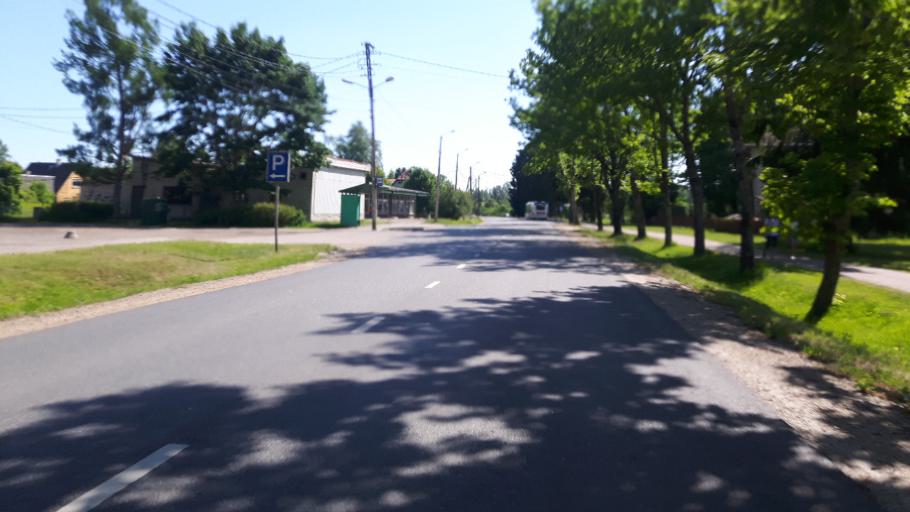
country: EE
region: Paernumaa
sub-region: Sindi linn
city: Sindi
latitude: 58.4033
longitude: 24.6470
